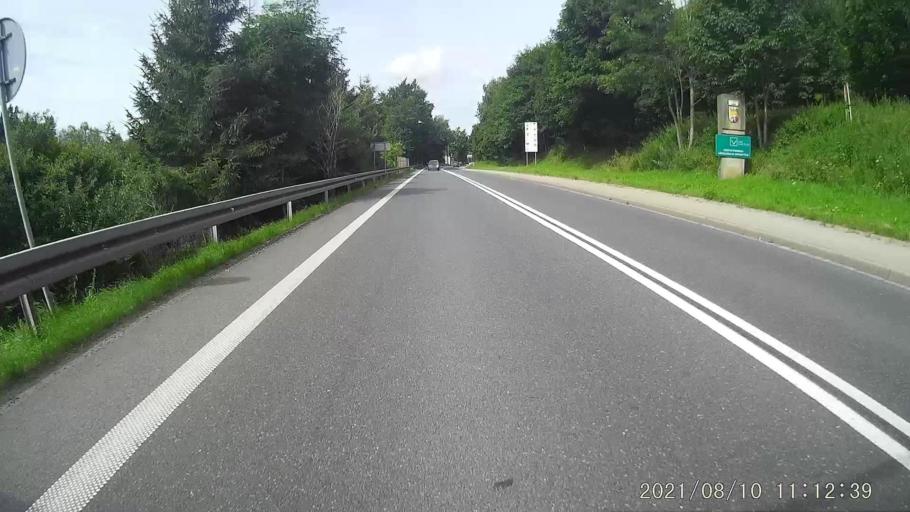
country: PL
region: Lower Silesian Voivodeship
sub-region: Powiat klodzki
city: Duszniki-Zdroj
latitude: 50.4047
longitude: 16.4033
